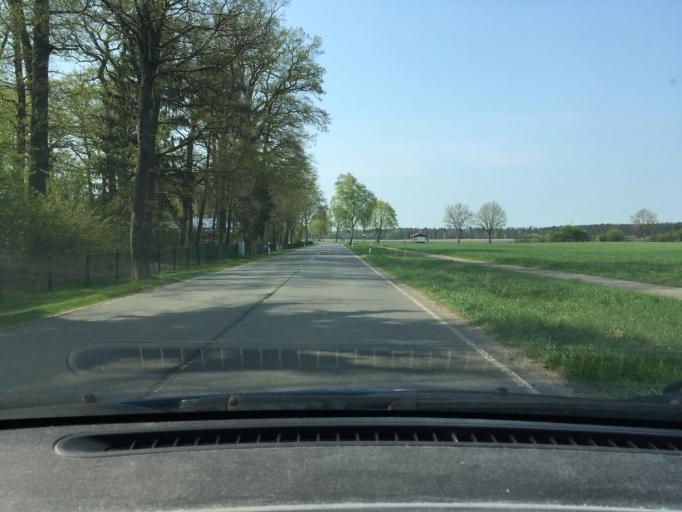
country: DE
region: Lower Saxony
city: Fassberg
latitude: 52.8812
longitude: 10.1904
